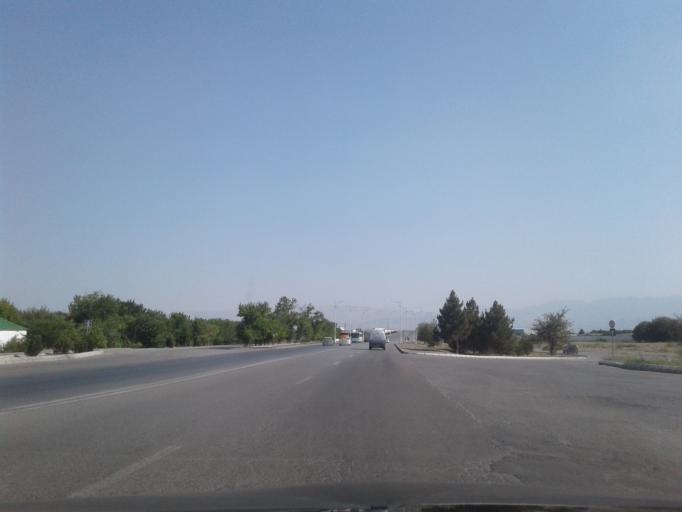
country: TM
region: Ahal
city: Ashgabat
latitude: 37.9689
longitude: 58.4225
